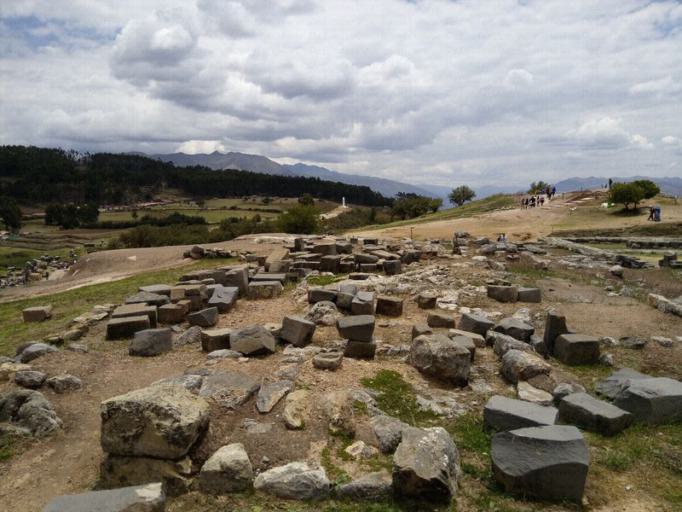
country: PE
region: Cusco
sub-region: Provincia de Cusco
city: Cusco
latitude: -13.5090
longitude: -71.9825
